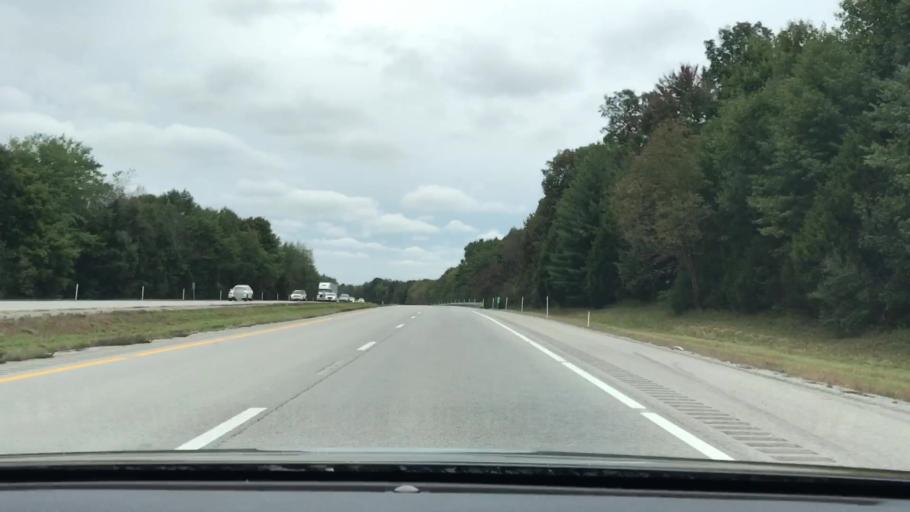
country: US
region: Kentucky
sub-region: Barren County
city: Cave City
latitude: 37.0395
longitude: -86.0625
